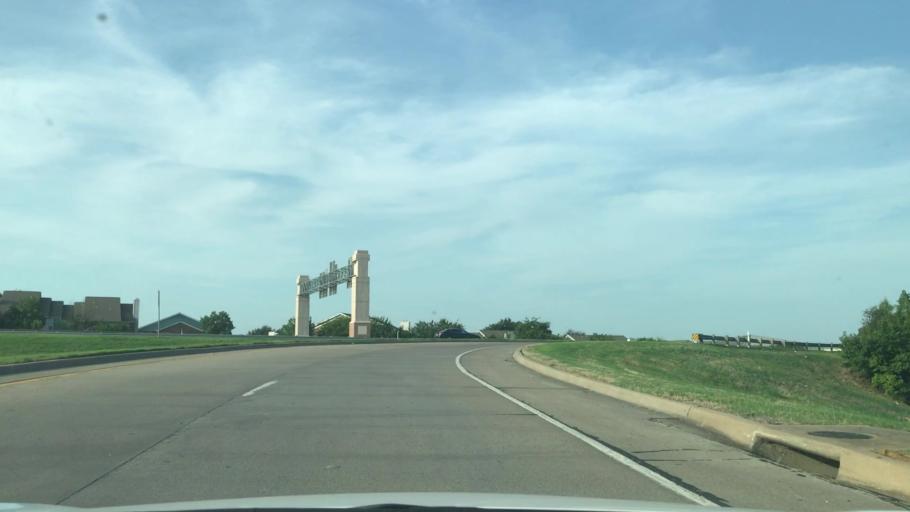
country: US
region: Texas
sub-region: Tarrant County
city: Arlington
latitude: 32.7606
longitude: -97.1190
